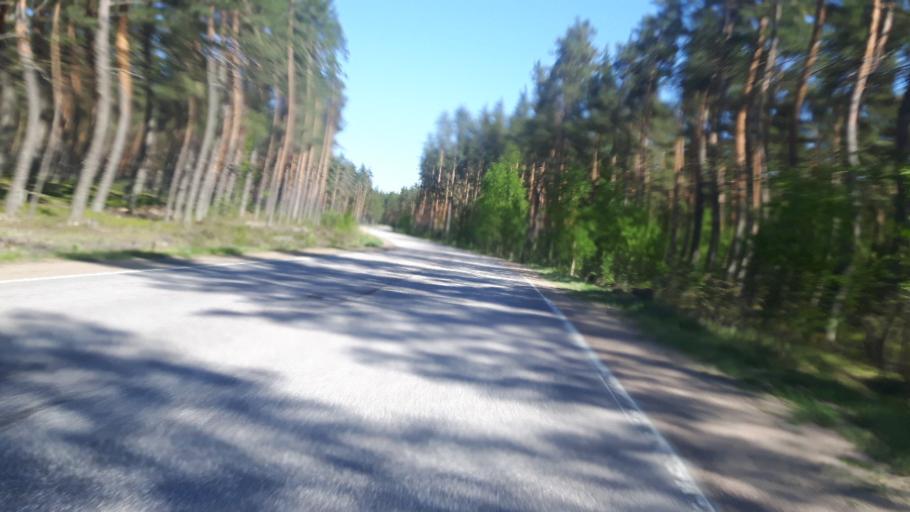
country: RU
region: Leningrad
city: Glebychevo
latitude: 60.2766
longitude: 28.9082
